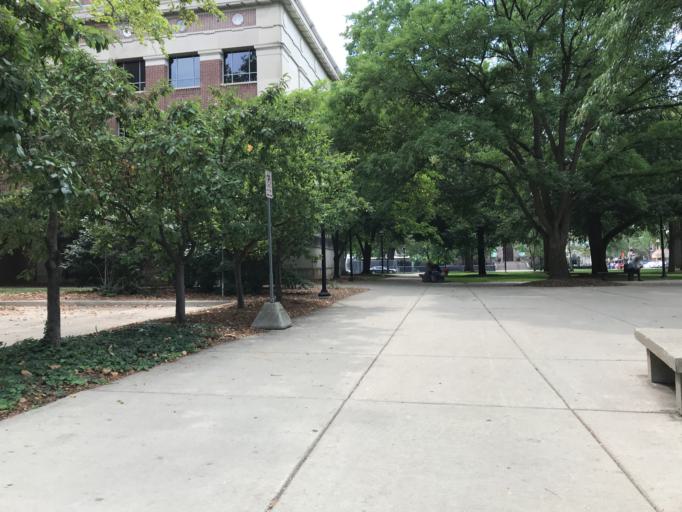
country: US
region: Michigan
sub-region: Washtenaw County
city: Ann Arbor
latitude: 42.2776
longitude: -83.7396
